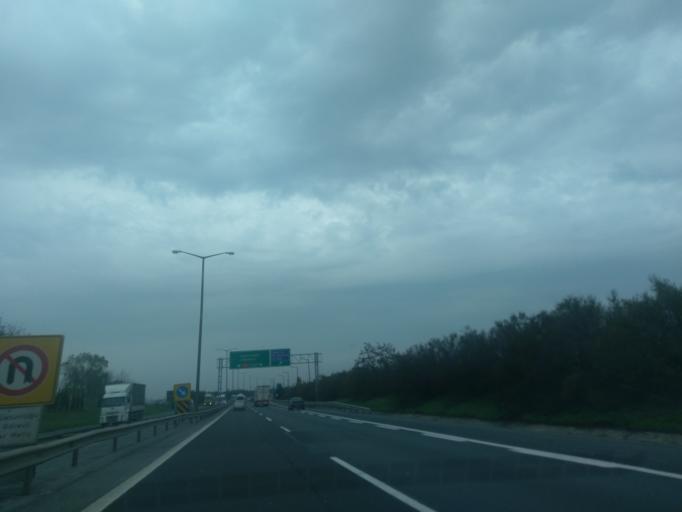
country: TR
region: Istanbul
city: Muratbey
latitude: 41.0833
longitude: 28.5080
